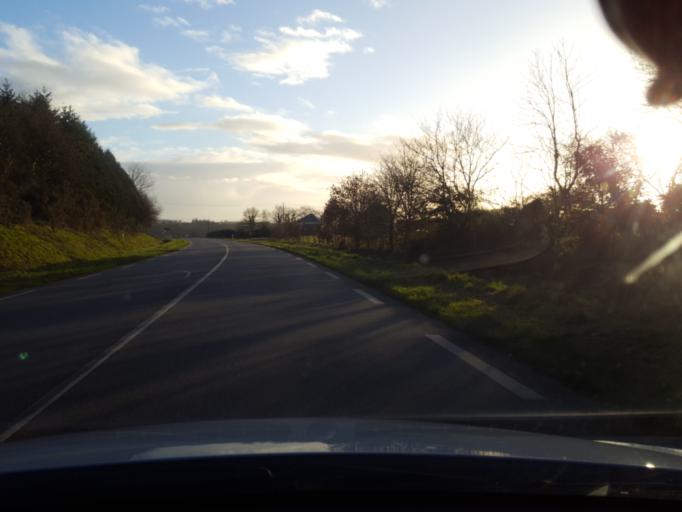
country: FR
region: Brittany
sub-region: Departement d'Ille-et-Vilaine
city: Guignen
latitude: 47.9285
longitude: -1.8519
